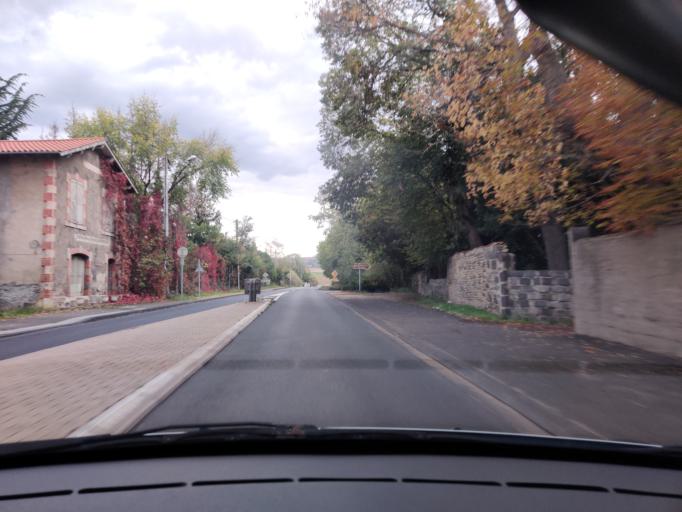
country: FR
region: Auvergne
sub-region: Departement du Puy-de-Dome
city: Saint-Bonnet-pres-Riom
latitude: 45.9477
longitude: 3.1091
